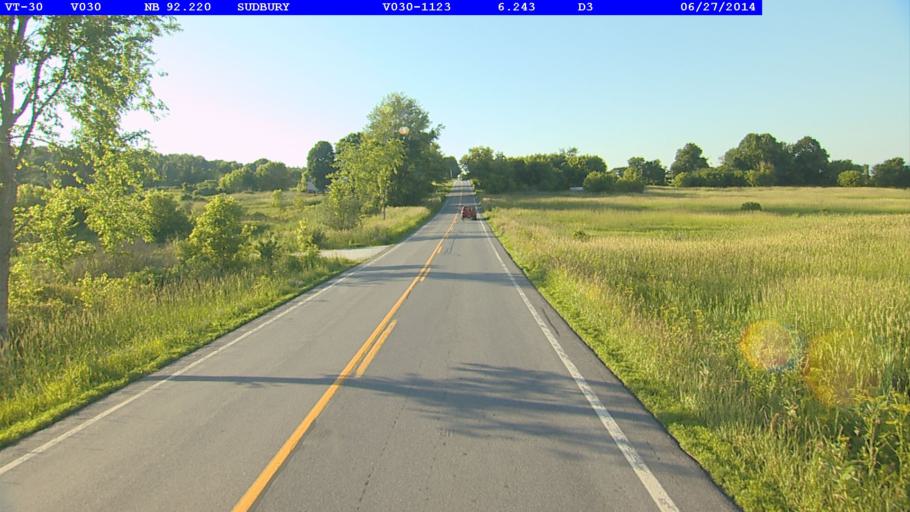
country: US
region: Vermont
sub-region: Rutland County
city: Brandon
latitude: 43.8361
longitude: -73.1944
